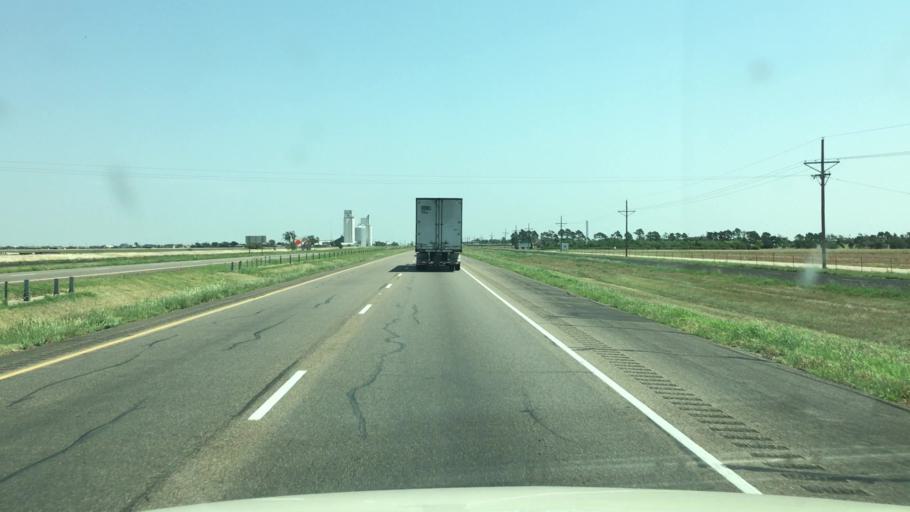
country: US
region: Texas
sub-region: Potter County
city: Bushland
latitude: 35.1916
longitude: -102.0823
